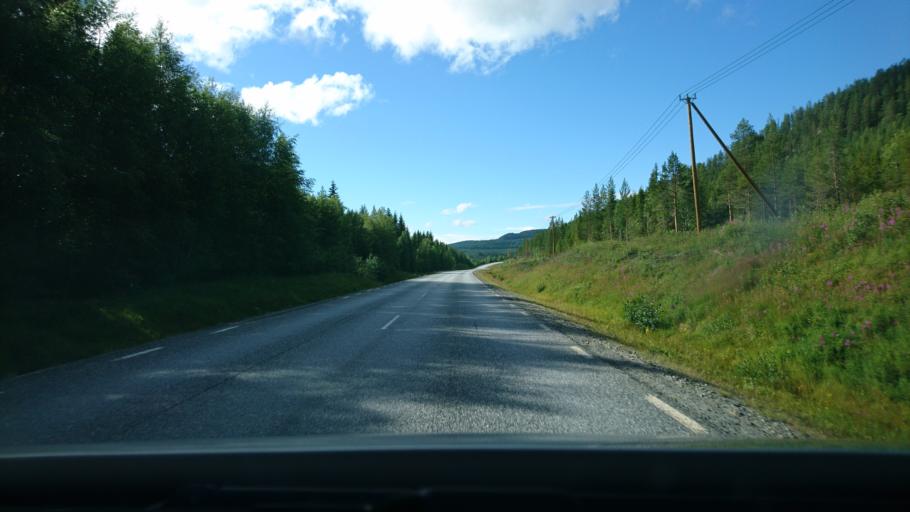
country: SE
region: Vaesterbotten
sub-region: Asele Kommun
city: Asele
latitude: 64.3131
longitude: 17.2250
